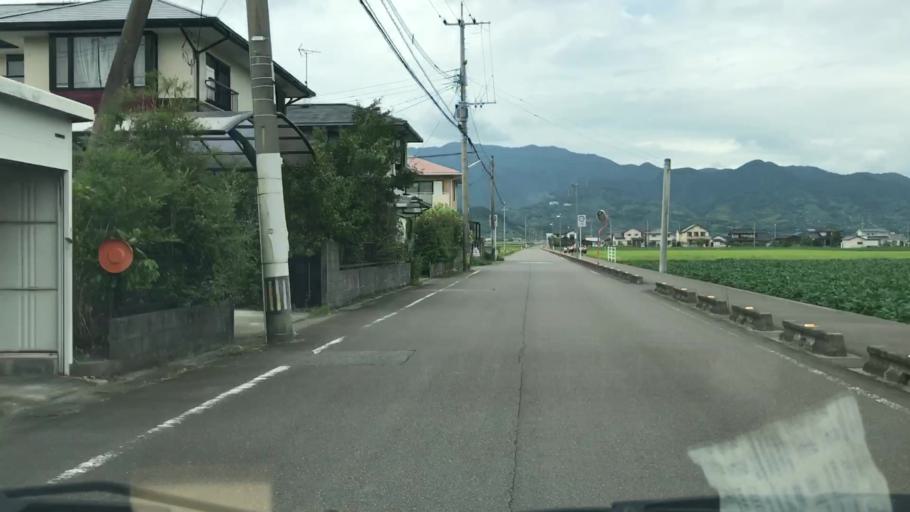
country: JP
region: Saga Prefecture
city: Saga-shi
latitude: 33.2825
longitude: 130.2262
